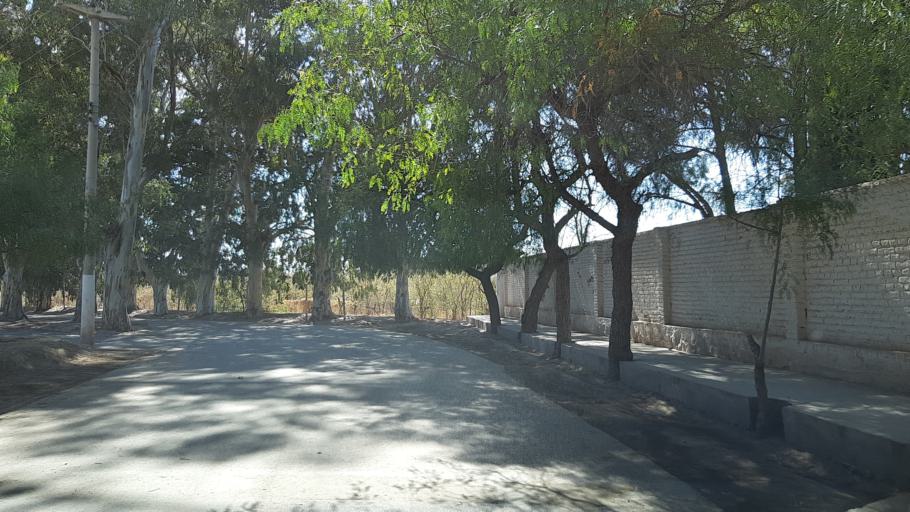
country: AR
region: San Juan
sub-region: Departamento de Zonda
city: Zonda
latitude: -31.5740
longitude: -68.7550
